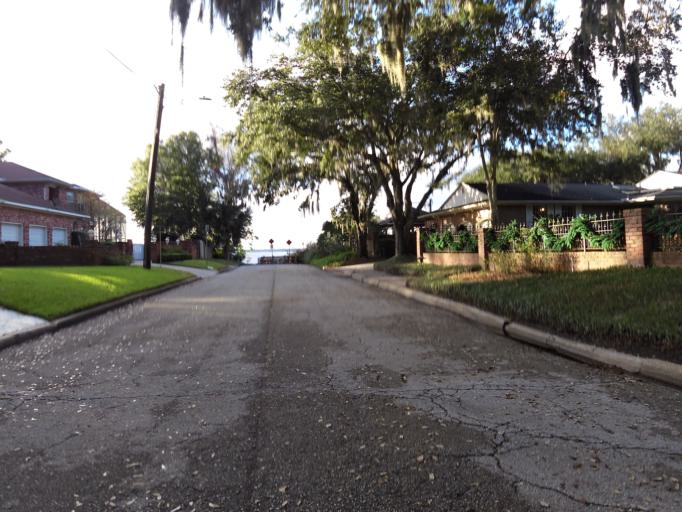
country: US
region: Florida
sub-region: Duval County
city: Jacksonville
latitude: 30.2922
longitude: -81.6546
